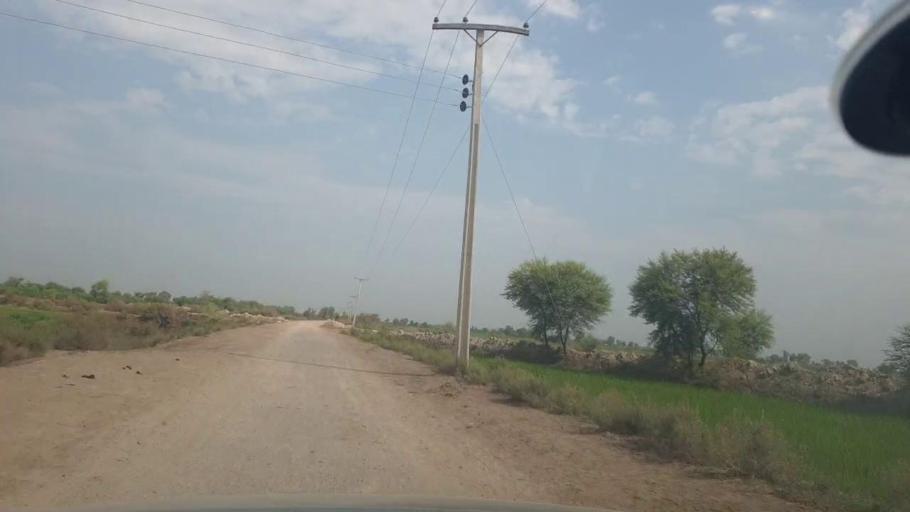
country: PK
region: Balochistan
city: Mehrabpur
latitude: 28.0629
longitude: 68.1043
